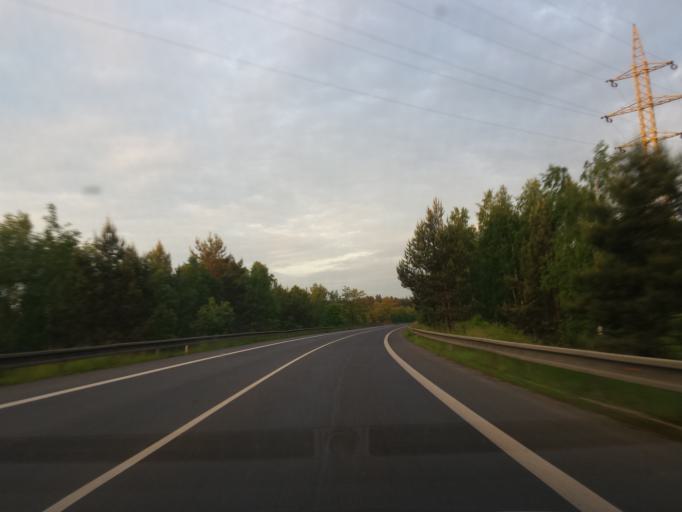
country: CZ
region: Liberecky
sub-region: Okres Ceska Lipa
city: Ceska Lipa
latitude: 50.6668
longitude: 14.5424
